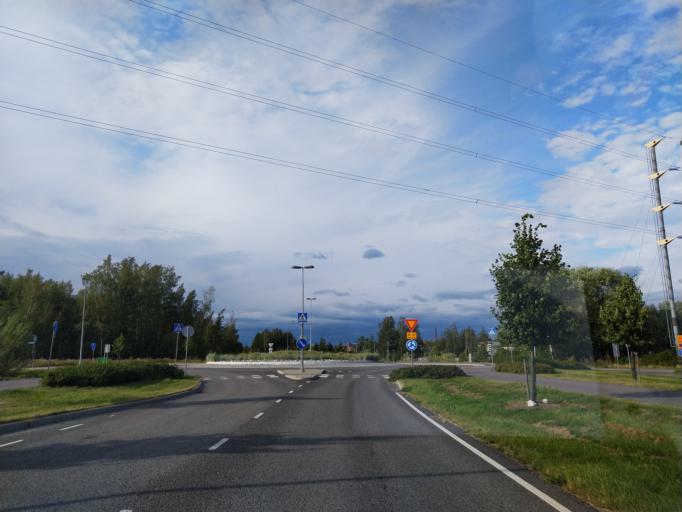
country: FI
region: Varsinais-Suomi
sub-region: Turku
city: Turku
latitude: 60.4211
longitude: 22.2275
